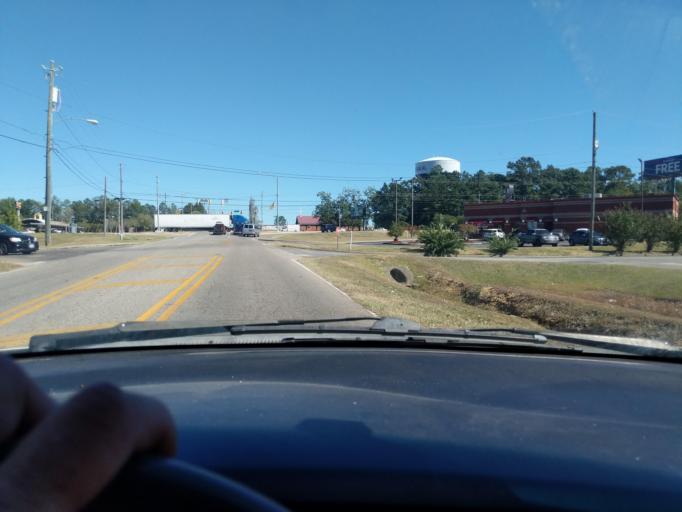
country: US
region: Alabama
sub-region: Houston County
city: Dothan
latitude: 31.1773
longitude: -85.4034
